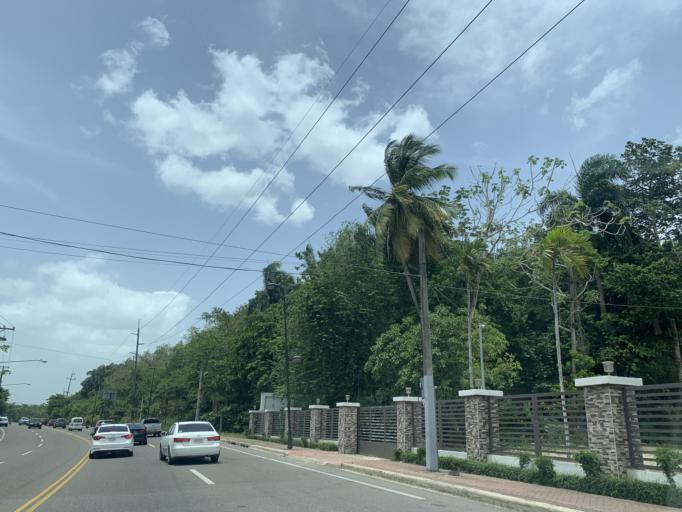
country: DO
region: Puerto Plata
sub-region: Puerto Plata
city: Puerto Plata
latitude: 19.7739
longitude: -70.6575
